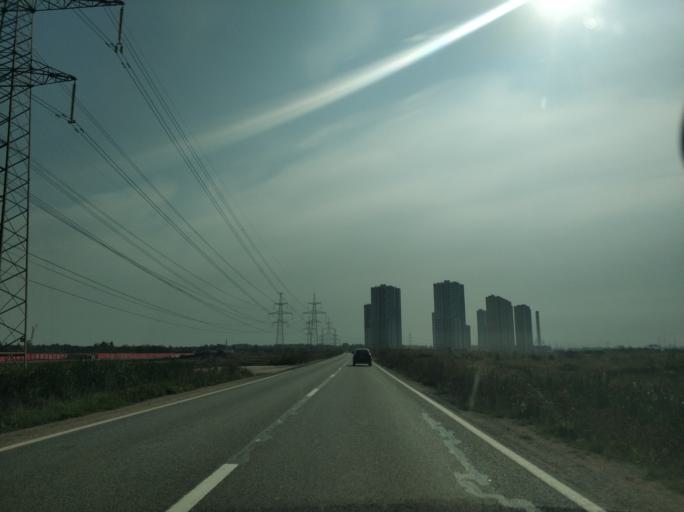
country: RU
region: Leningrad
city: Murino
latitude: 60.0160
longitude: 30.4734
